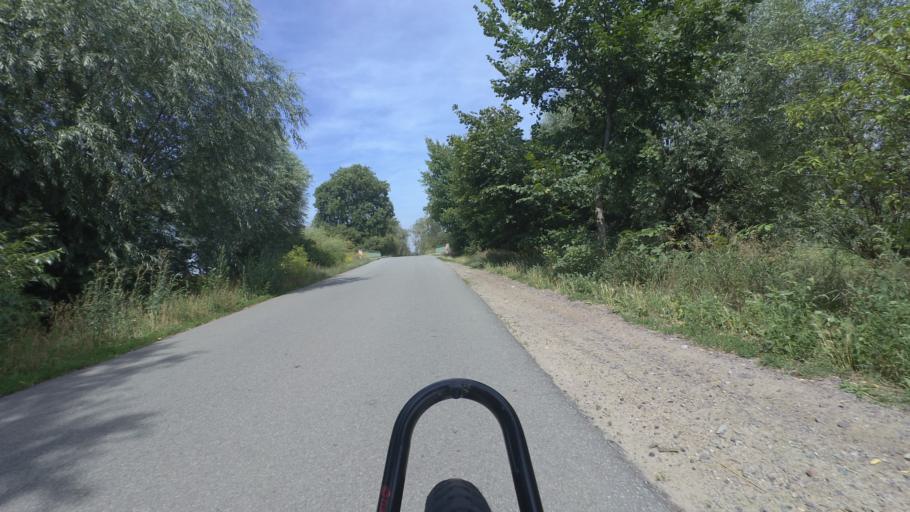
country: DE
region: Brandenburg
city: Rhinow
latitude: 52.7581
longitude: 12.3333
